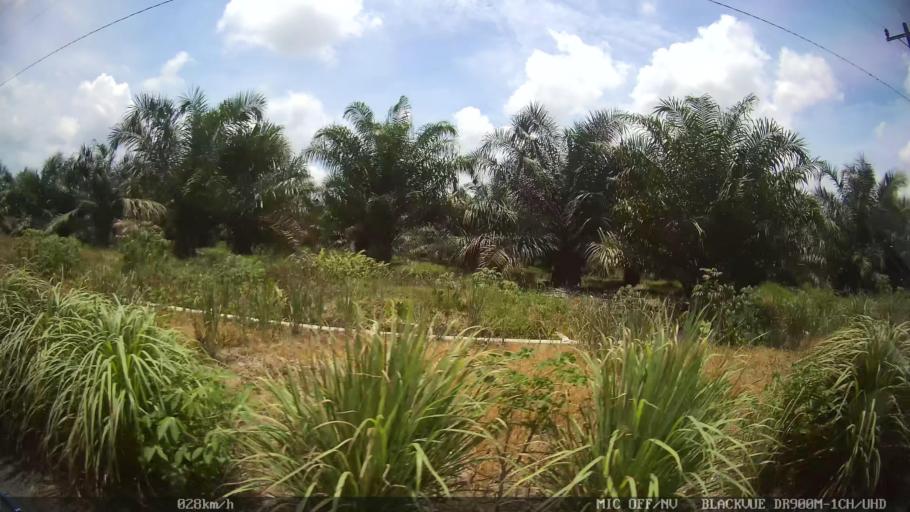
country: ID
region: North Sumatra
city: Percut
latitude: 3.5409
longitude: 98.8652
